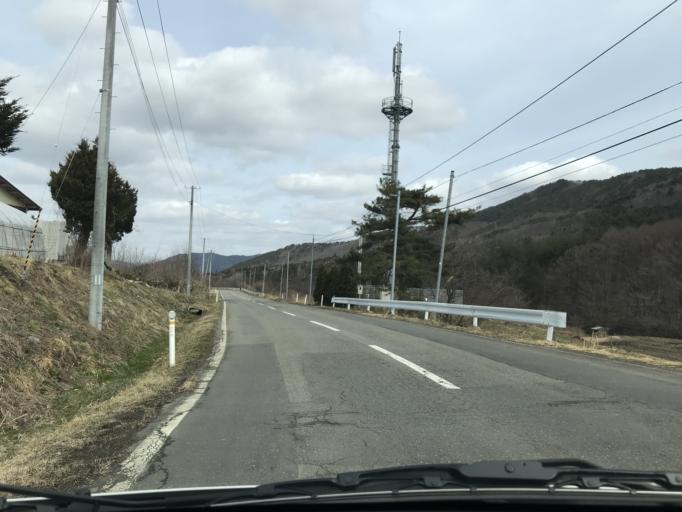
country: JP
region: Iwate
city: Kitakami
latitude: 39.2669
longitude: 141.3209
